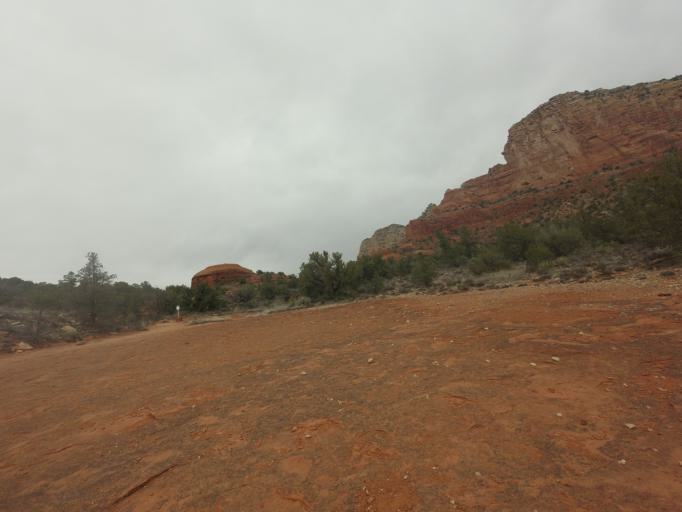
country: US
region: Arizona
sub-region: Yavapai County
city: Village of Oak Creek (Big Park)
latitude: 34.8042
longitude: -111.7481
